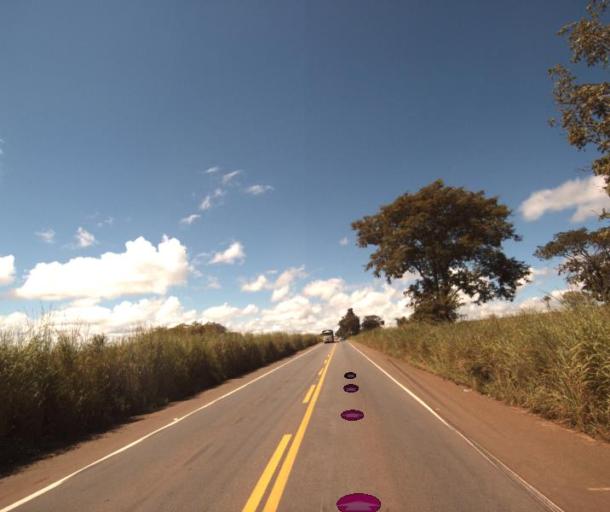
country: BR
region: Goias
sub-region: Jaragua
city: Jaragua
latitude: -15.8182
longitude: -49.2881
